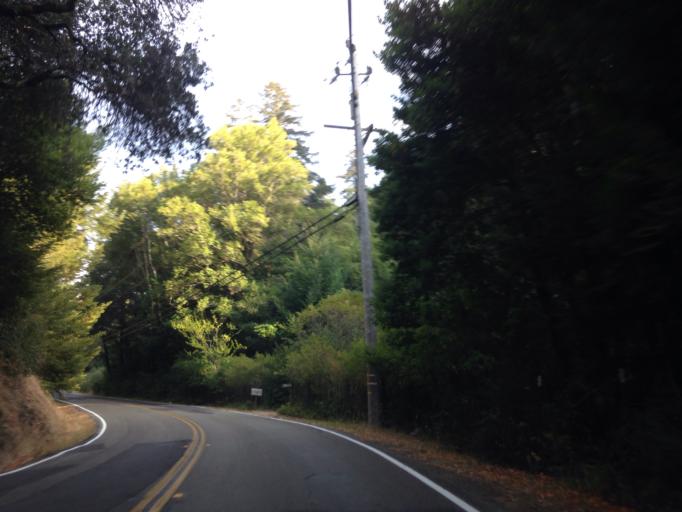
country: US
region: California
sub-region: Marin County
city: Woodacre
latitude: 38.0526
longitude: -122.6473
